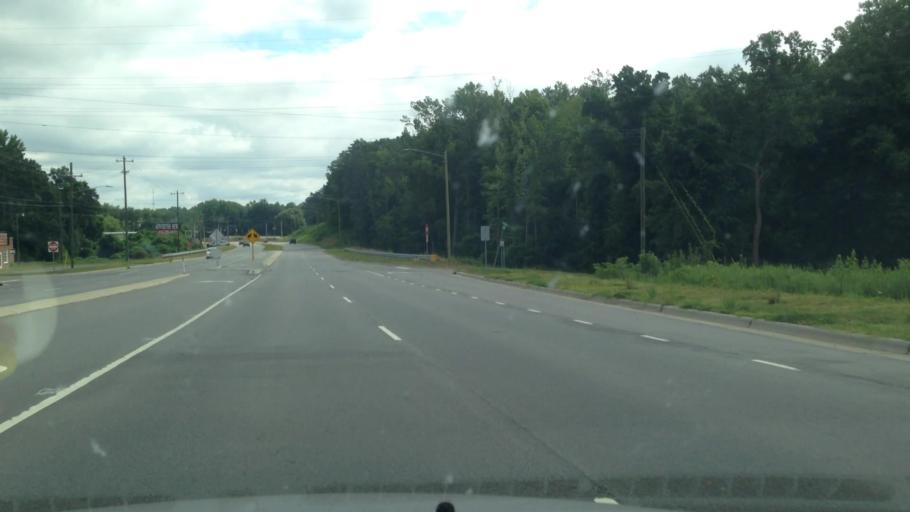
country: US
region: North Carolina
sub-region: Rockingham County
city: Reidsville
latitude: 36.3614
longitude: -79.6854
